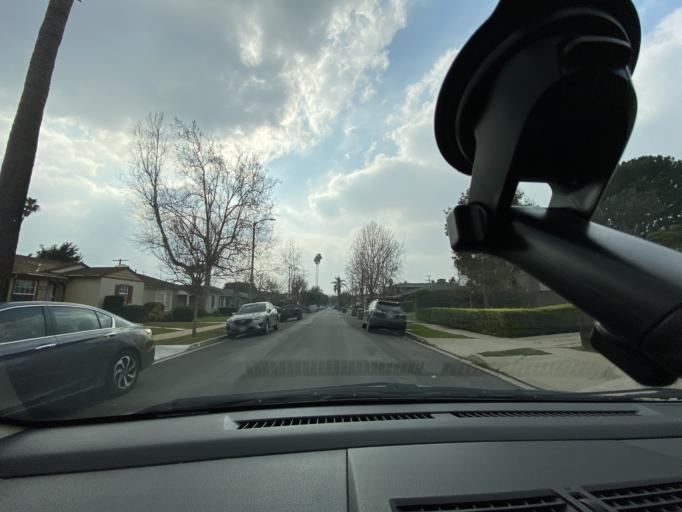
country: US
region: California
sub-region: Los Angeles County
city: Culver City
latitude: 34.0351
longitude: -118.3973
